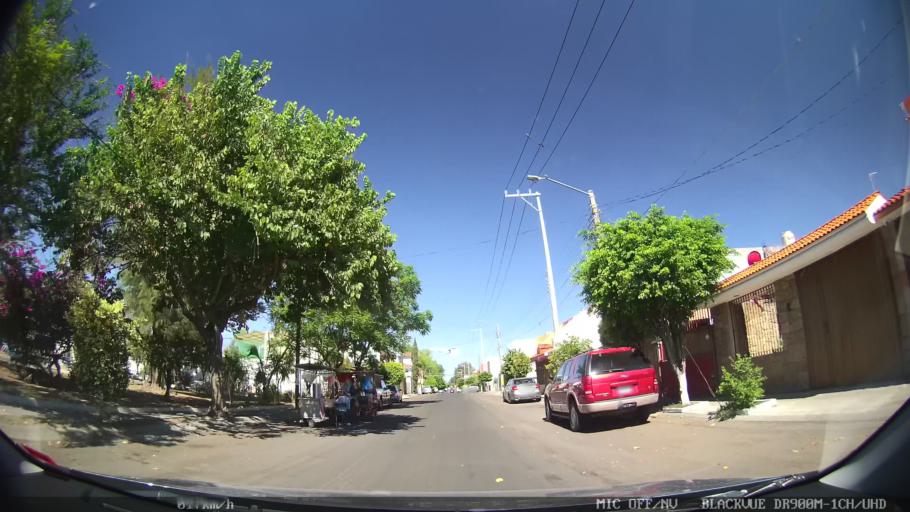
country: MX
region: Jalisco
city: Tlaquepaque
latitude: 20.6578
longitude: -103.2967
